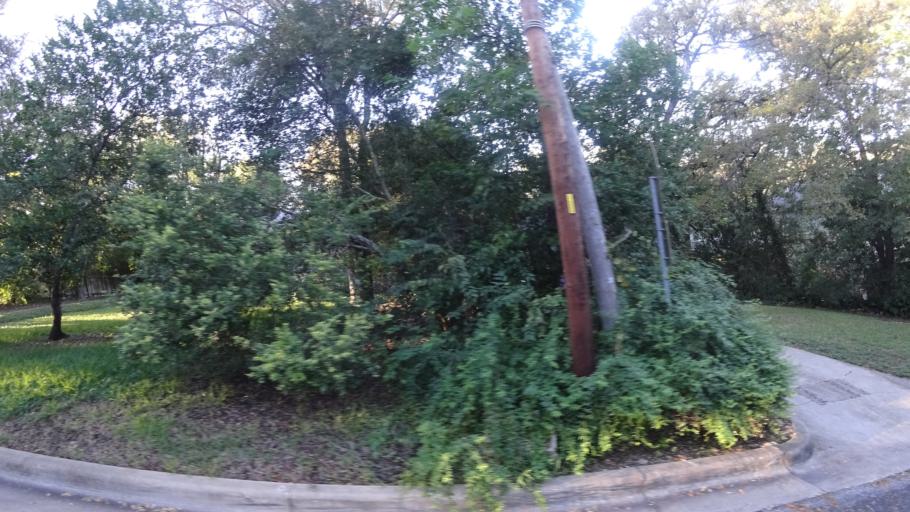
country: US
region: Texas
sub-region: Travis County
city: West Lake Hills
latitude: 30.3020
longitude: -97.7787
